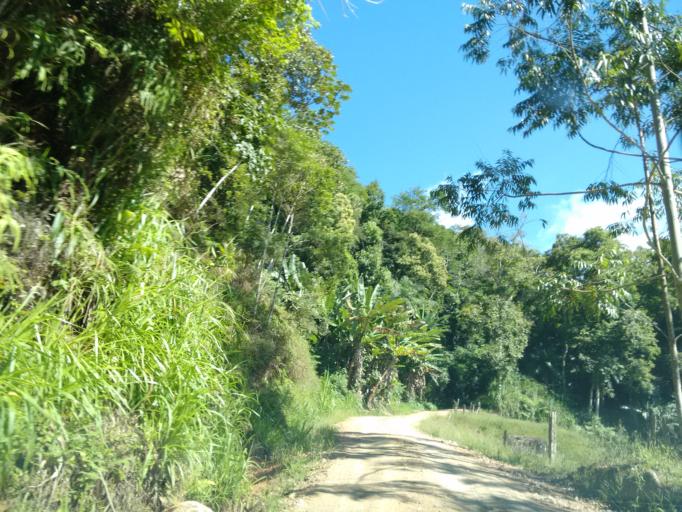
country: BR
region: Santa Catarina
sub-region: Pomerode
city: Pomerode
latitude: -26.7538
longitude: -49.1893
